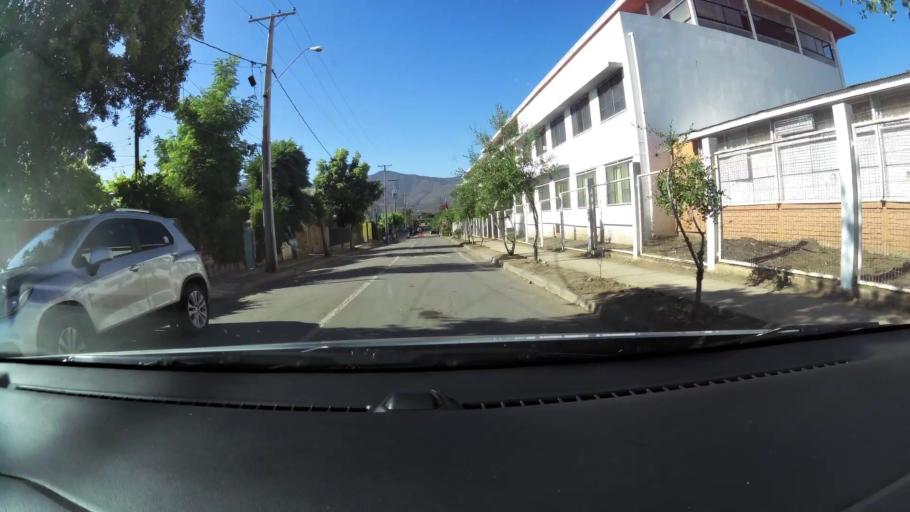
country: CL
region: Santiago Metropolitan
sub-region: Provincia de Chacabuco
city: Lampa
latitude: -33.3987
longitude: -71.1306
